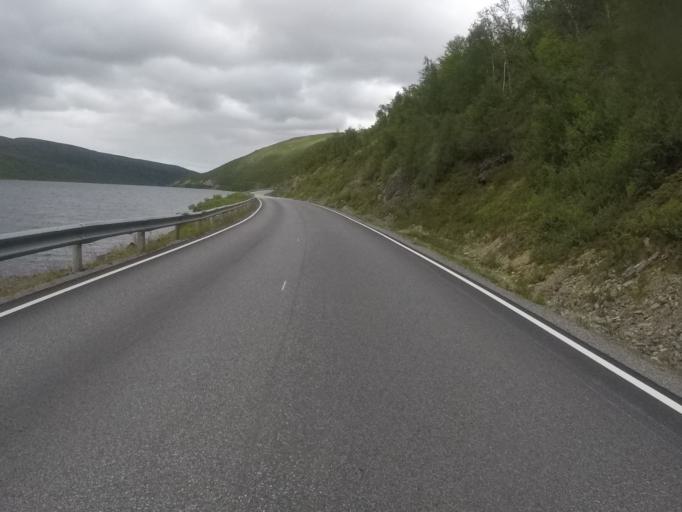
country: NO
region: Finnmark Fylke
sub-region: Alta
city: Alta
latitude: 69.6859
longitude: 23.4277
